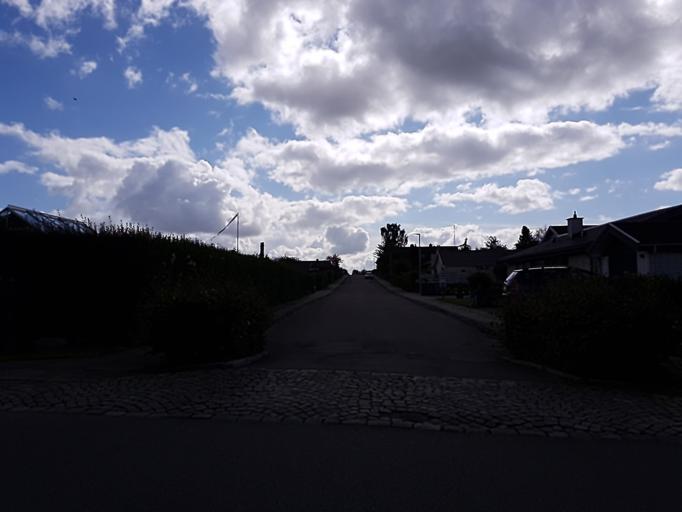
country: DK
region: Capital Region
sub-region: Egedal Kommune
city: Olstykke
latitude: 55.7923
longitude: 12.1434
